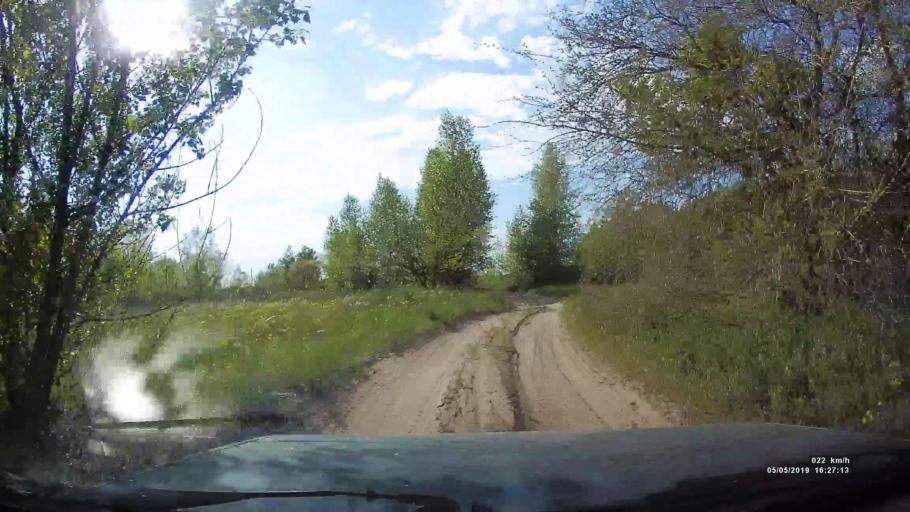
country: RU
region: Rostov
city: Ust'-Donetskiy
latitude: 47.7646
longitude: 41.0196
